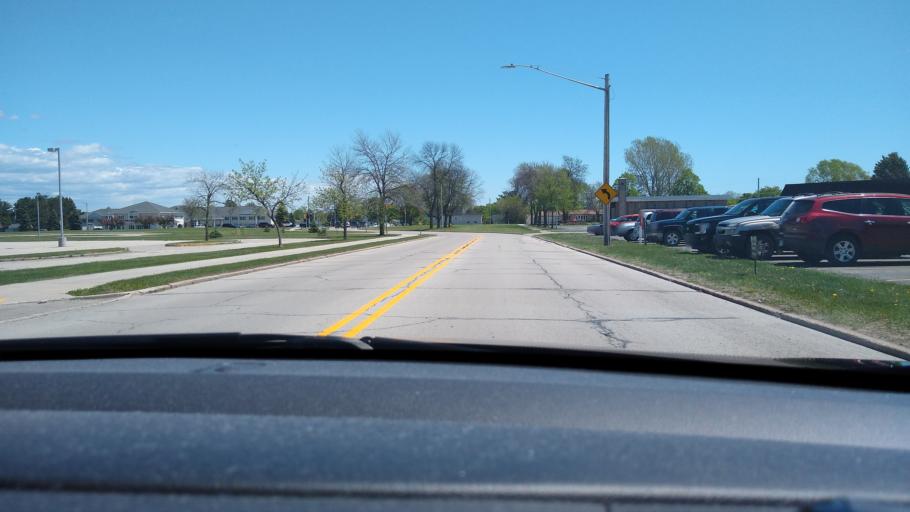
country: US
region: Michigan
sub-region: Delta County
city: Escanaba
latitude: 45.7391
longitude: -87.0826
